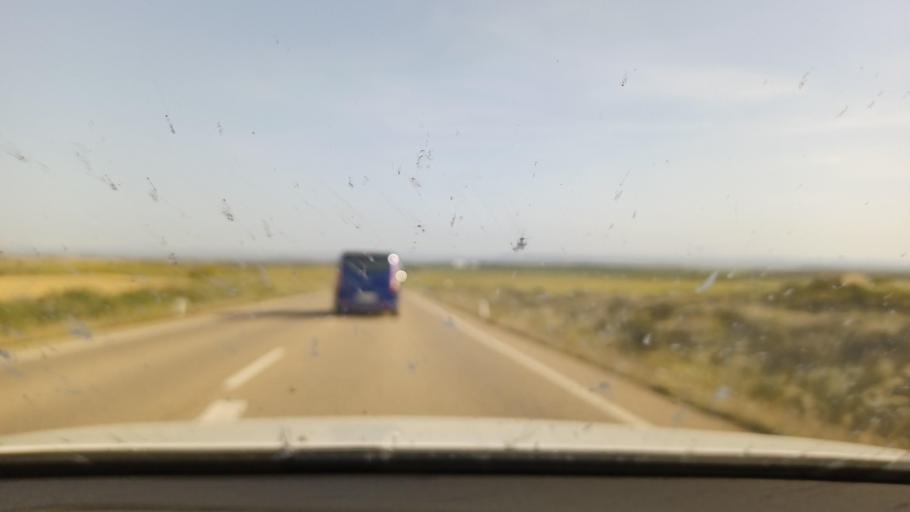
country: ES
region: Aragon
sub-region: Provincia de Zaragoza
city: Chiprana
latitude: 41.3179
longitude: -0.0770
